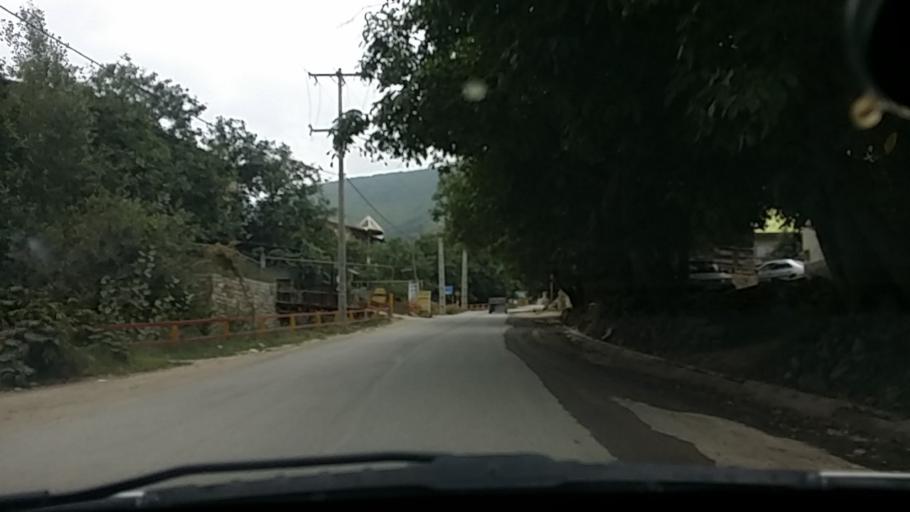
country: IR
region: Mazandaran
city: `Abbasabad
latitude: 36.4852
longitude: 51.1334
